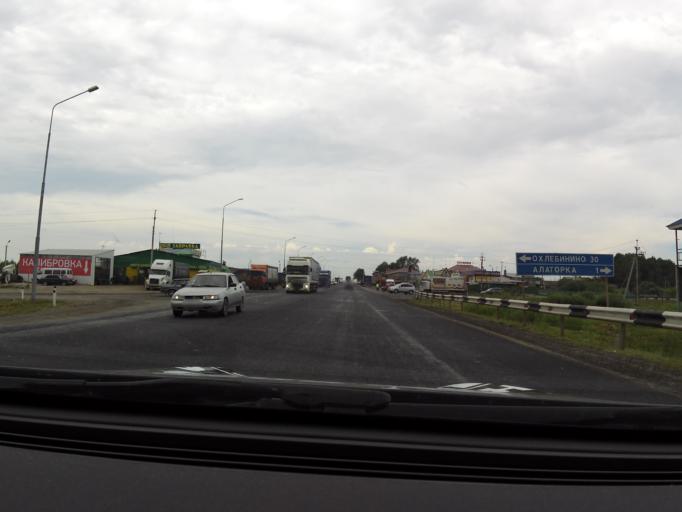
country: RU
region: Bashkortostan
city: Iglino
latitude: 54.7614
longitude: 56.3948
